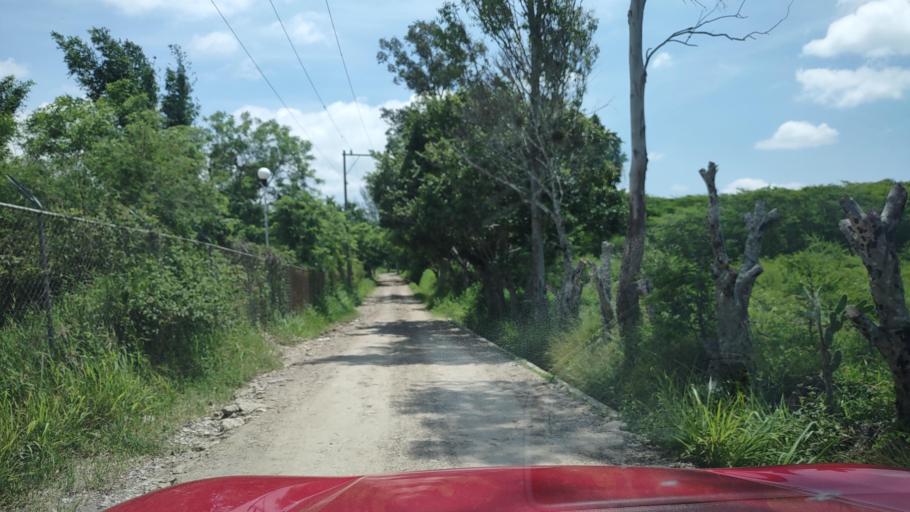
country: MX
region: Veracruz
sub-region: Emiliano Zapata
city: Dos Rios
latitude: 19.4636
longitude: -96.7886
